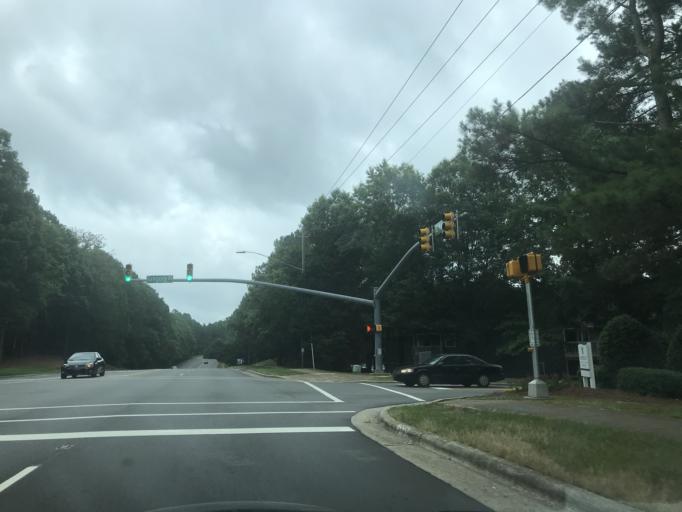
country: US
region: North Carolina
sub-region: Wake County
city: Cary
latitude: 35.8030
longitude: -78.7750
